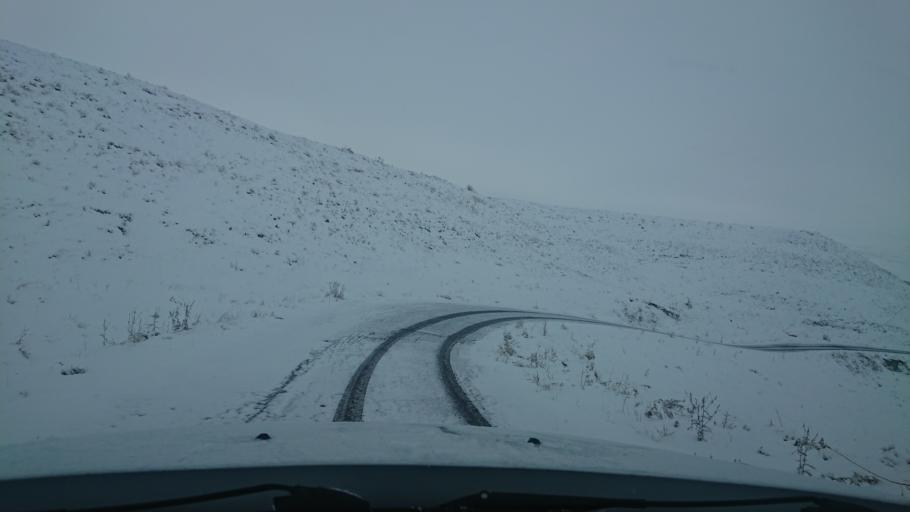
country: TR
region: Aksaray
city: Acipinar
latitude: 38.6727
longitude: 33.8632
